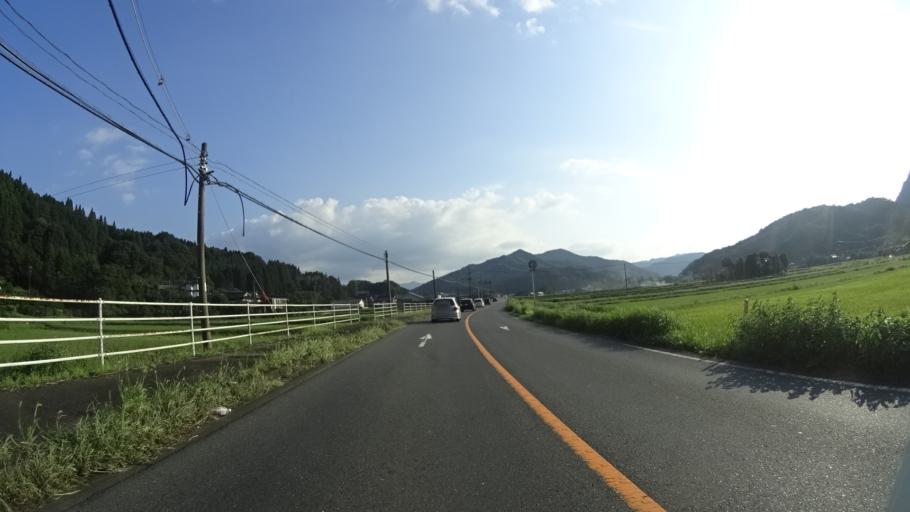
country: JP
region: Oita
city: Bungo-Takada-shi
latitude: 33.4599
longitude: 131.3310
